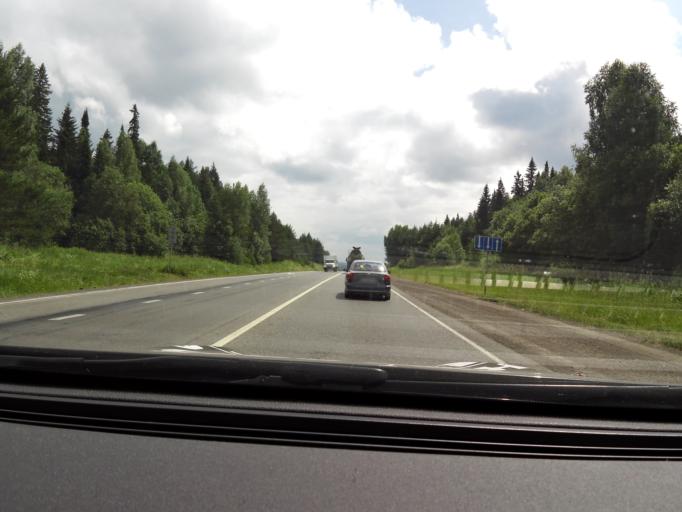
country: RU
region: Perm
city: Kungur
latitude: 57.3202
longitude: 56.9656
